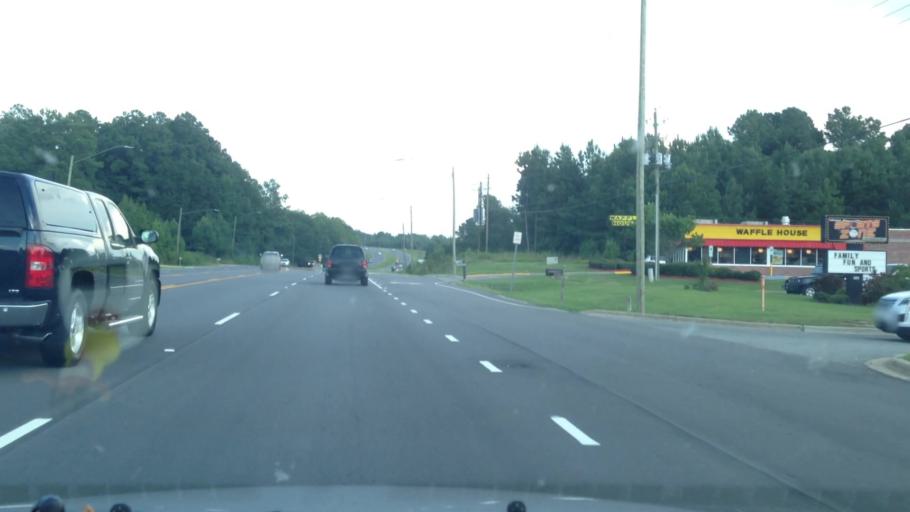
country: US
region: North Carolina
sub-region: Harnett County
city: Lillington
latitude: 35.4157
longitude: -78.7991
